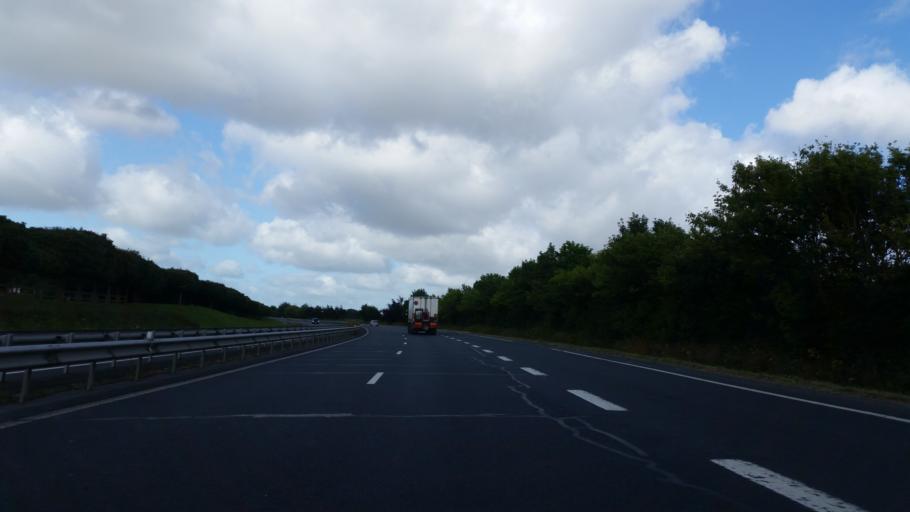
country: FR
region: Lower Normandy
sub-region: Departement du Calvados
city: Grandcamp-Maisy
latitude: 49.3434
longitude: -1.0224
